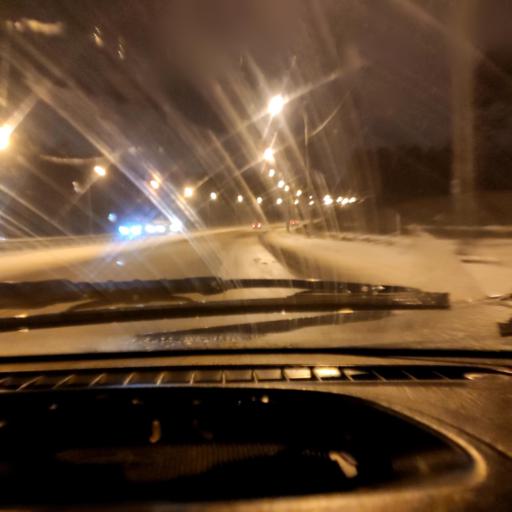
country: RU
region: Samara
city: Zhigulevsk
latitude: 53.5320
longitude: 49.5179
